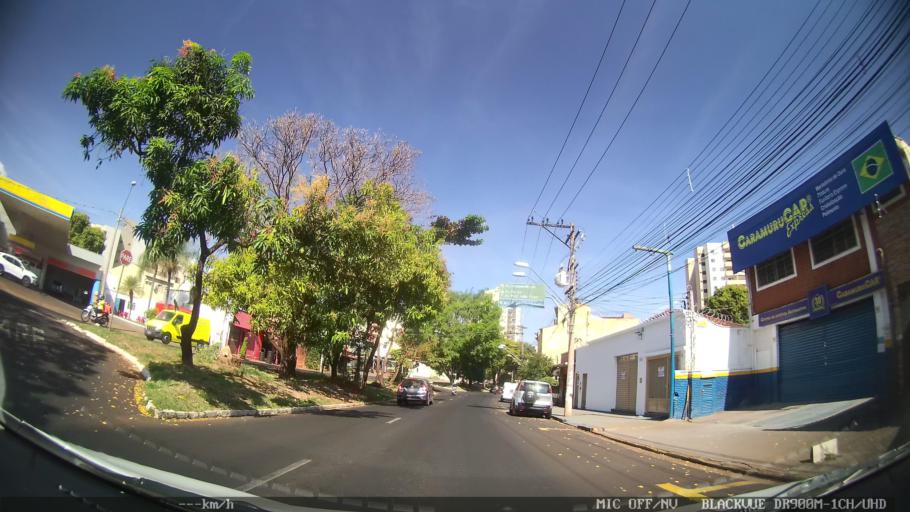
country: BR
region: Sao Paulo
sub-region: Ribeirao Preto
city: Ribeirao Preto
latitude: -21.1885
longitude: -47.8200
